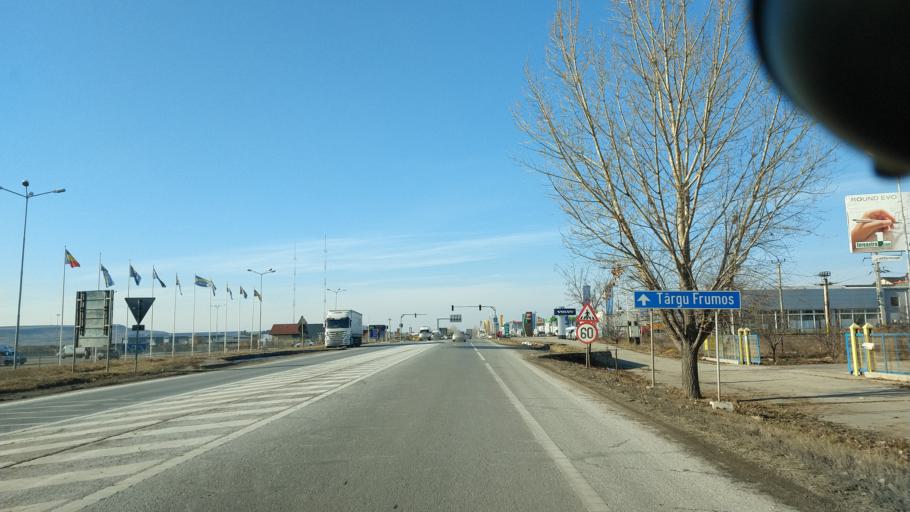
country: RO
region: Iasi
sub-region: Comuna Valea Lupului
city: Valea Lupului
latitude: 47.1814
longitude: 27.4710
